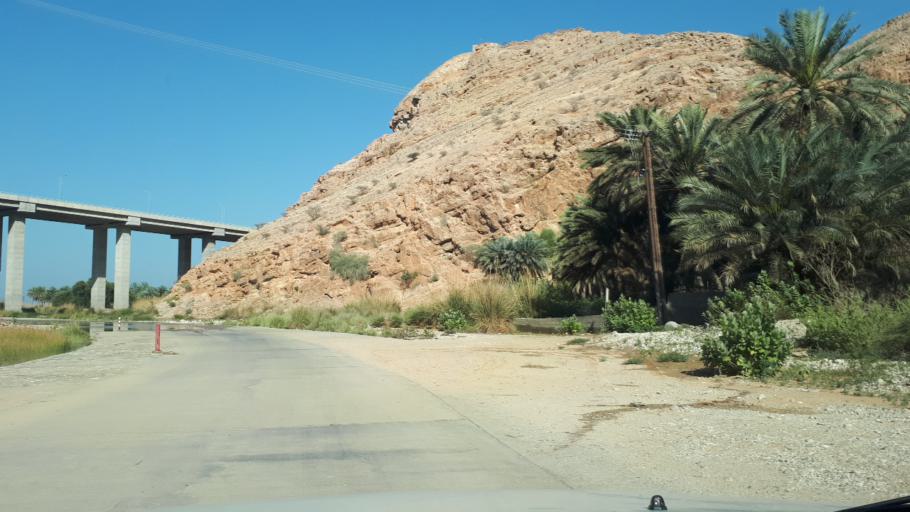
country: OM
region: Ash Sharqiyah
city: Sur
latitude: 22.8230
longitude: 59.2591
